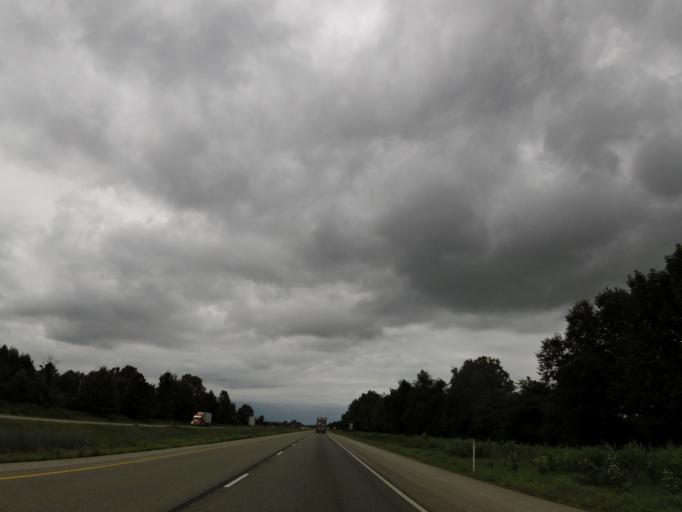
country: US
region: Illinois
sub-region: Massac County
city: Metropolis
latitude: 37.1692
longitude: -88.6824
